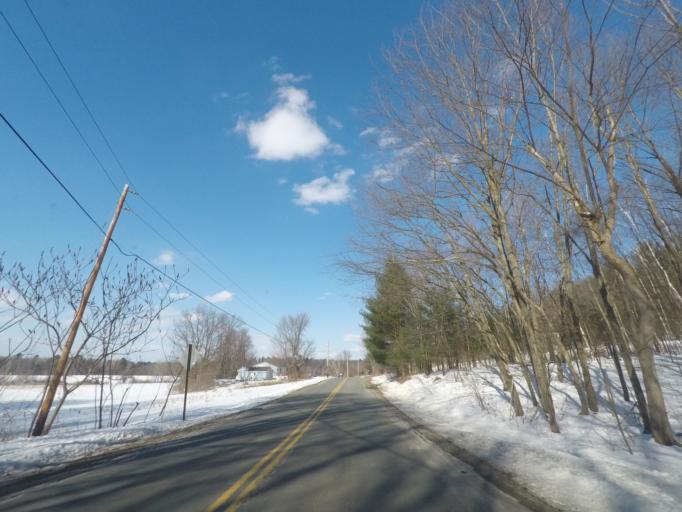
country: US
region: New York
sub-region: Saratoga County
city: Stillwater
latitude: 42.8776
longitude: -73.5795
